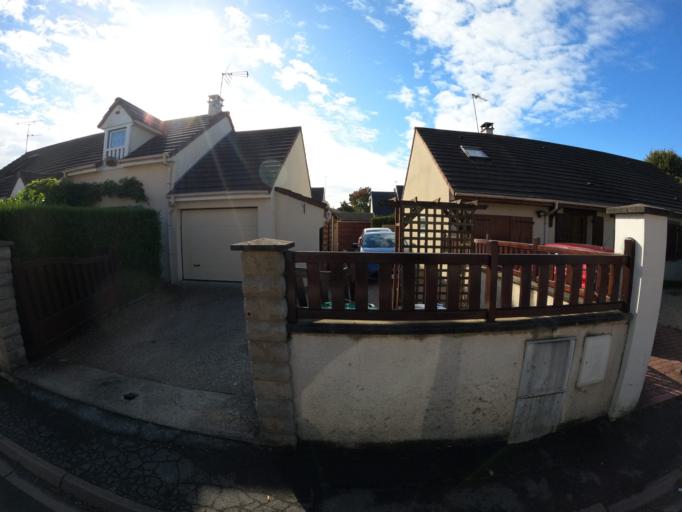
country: FR
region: Ile-de-France
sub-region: Departement de Seine-et-Marne
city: Saint-Germain-sur-Morin
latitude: 48.8809
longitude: 2.8477
